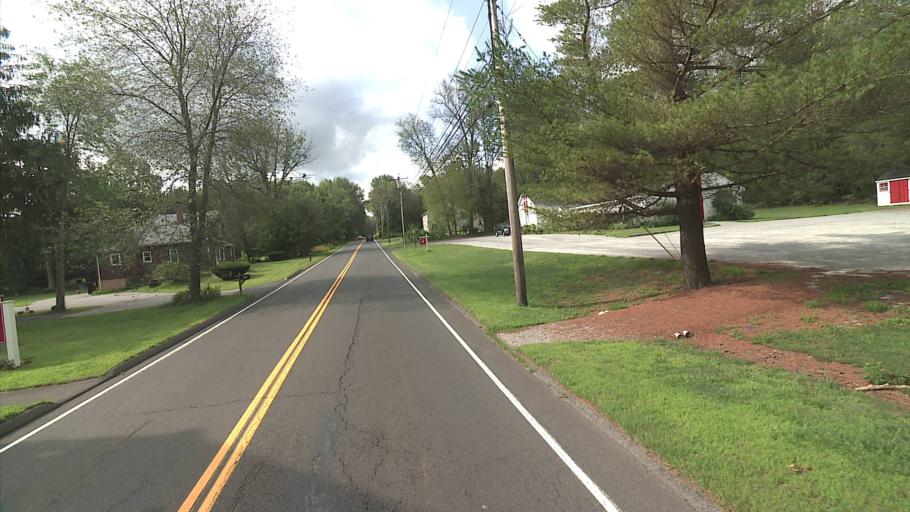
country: US
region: Connecticut
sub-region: Middlesex County
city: Higganum
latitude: 41.4637
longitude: -72.5561
